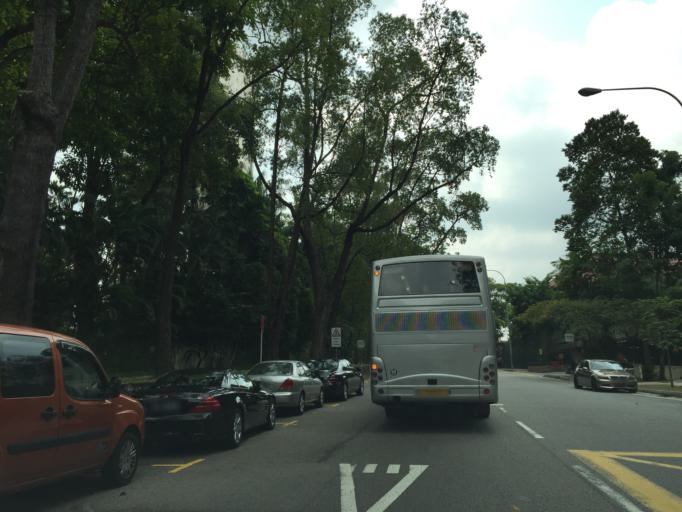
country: SG
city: Singapore
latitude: 1.3076
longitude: 103.8315
